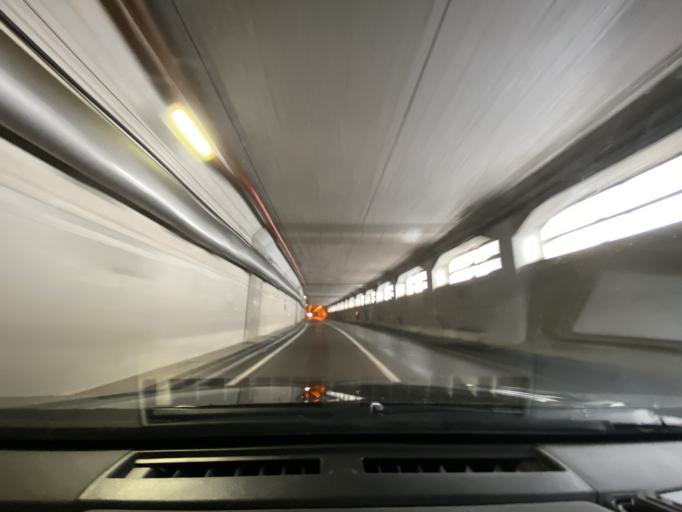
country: JP
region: Hokkaido
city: Rumoi
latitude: 43.7970
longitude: 141.3770
